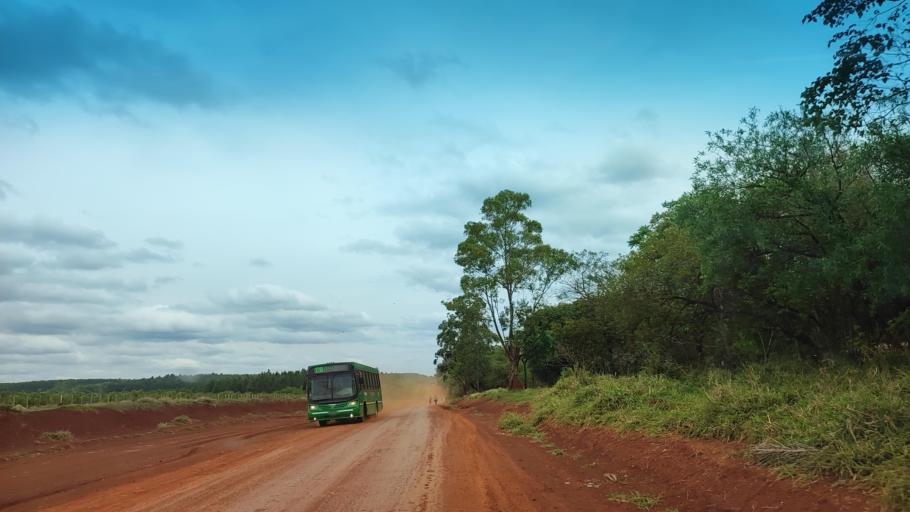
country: AR
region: Misiones
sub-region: Departamento de Capital
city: Posadas
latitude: -27.4863
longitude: -55.9708
